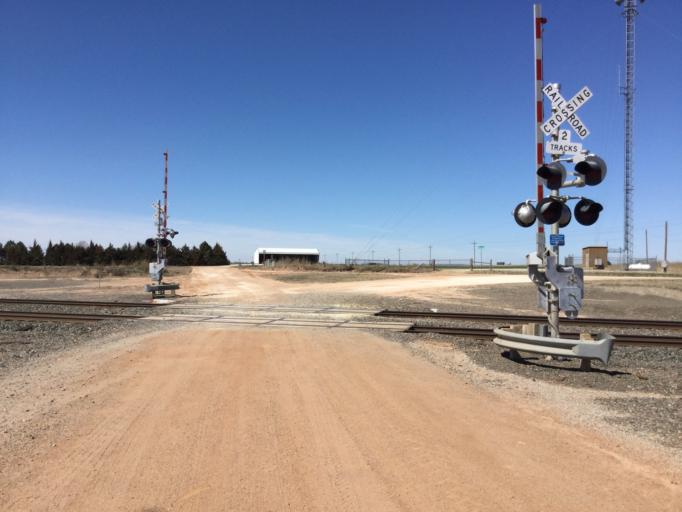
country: US
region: Kansas
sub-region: Barber County
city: Kiowa
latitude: 37.0244
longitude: -98.4866
